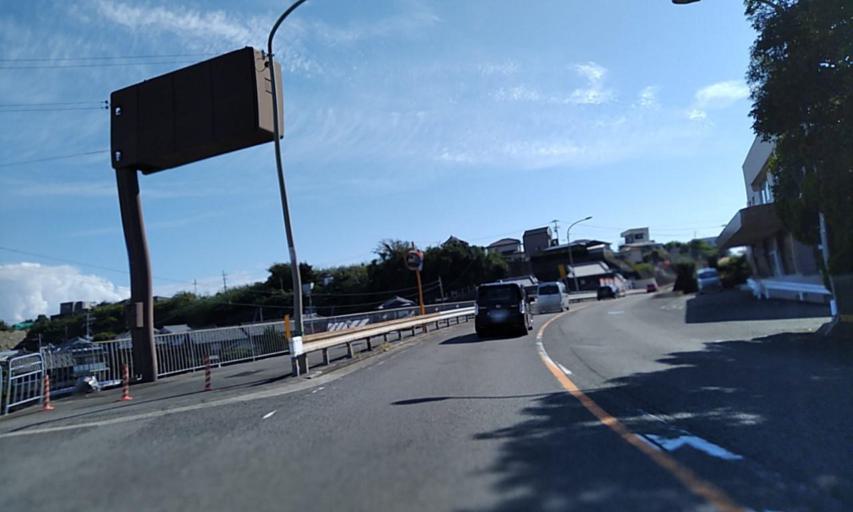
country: JP
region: Wakayama
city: Gobo
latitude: 33.8127
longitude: 135.2191
